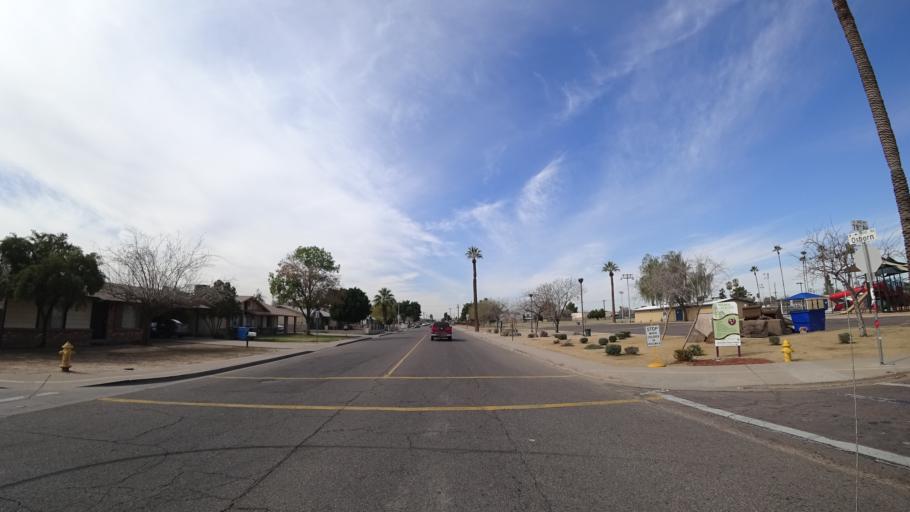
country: US
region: Arizona
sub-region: Maricopa County
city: Tolleson
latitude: 33.4873
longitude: -112.2269
